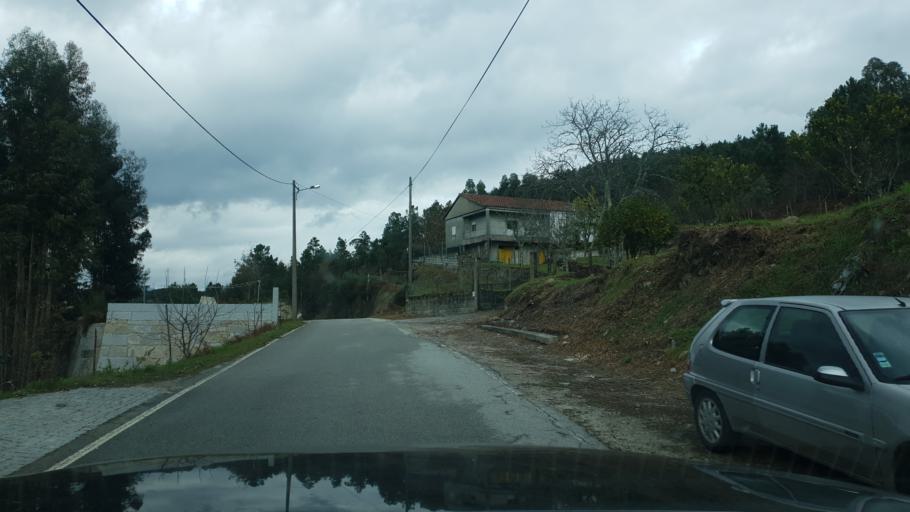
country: PT
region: Viseu
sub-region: Castro Daire
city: Castro Daire
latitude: 40.8812
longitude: -8.0123
